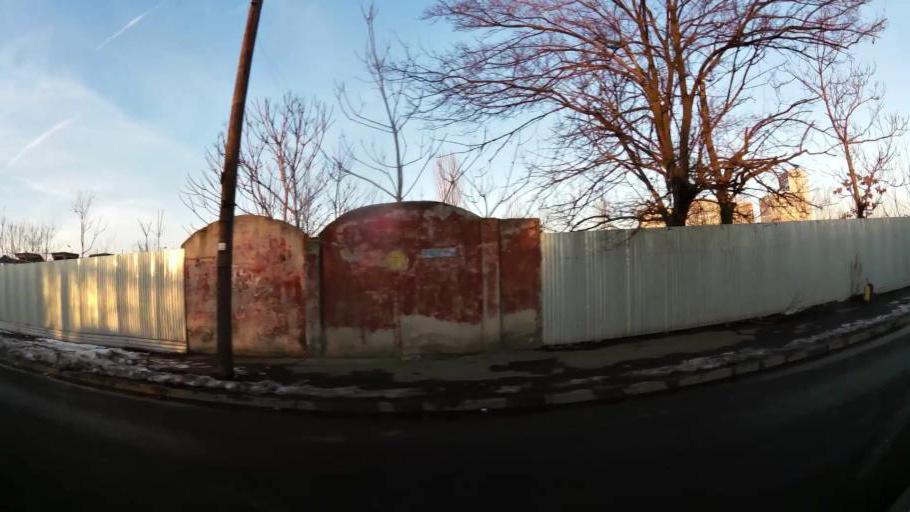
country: RO
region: Ilfov
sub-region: Comuna Fundeni-Dobroesti
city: Fundeni
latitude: 44.4502
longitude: 26.1407
